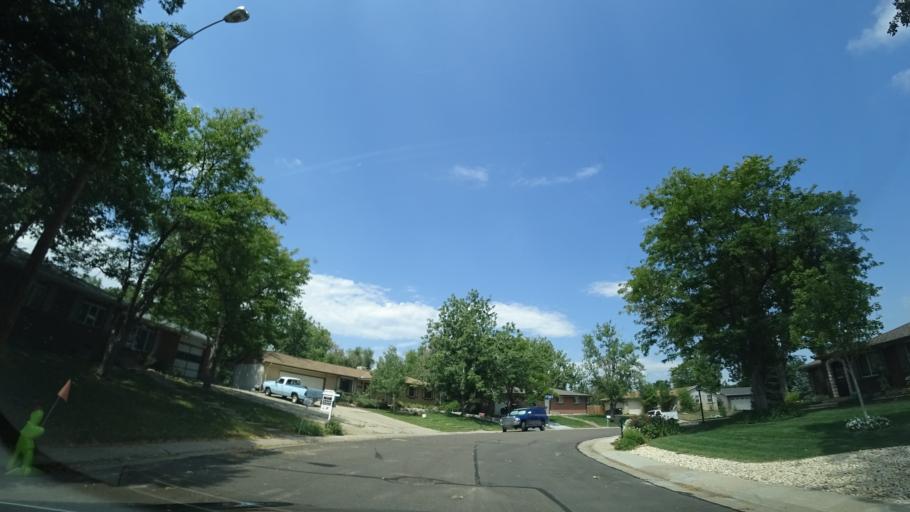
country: US
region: Colorado
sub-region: Jefferson County
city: Lakewood
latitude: 39.7156
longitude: -105.0735
